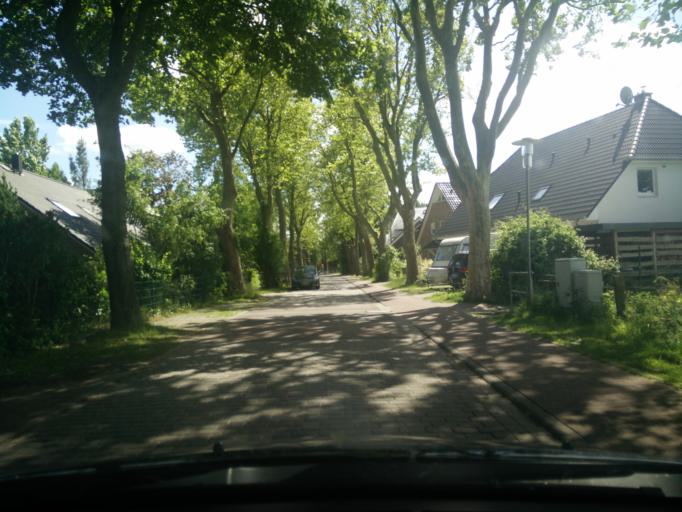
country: DE
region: Schleswig-Holstein
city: Prisdorf
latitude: 53.6767
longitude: 9.7607
